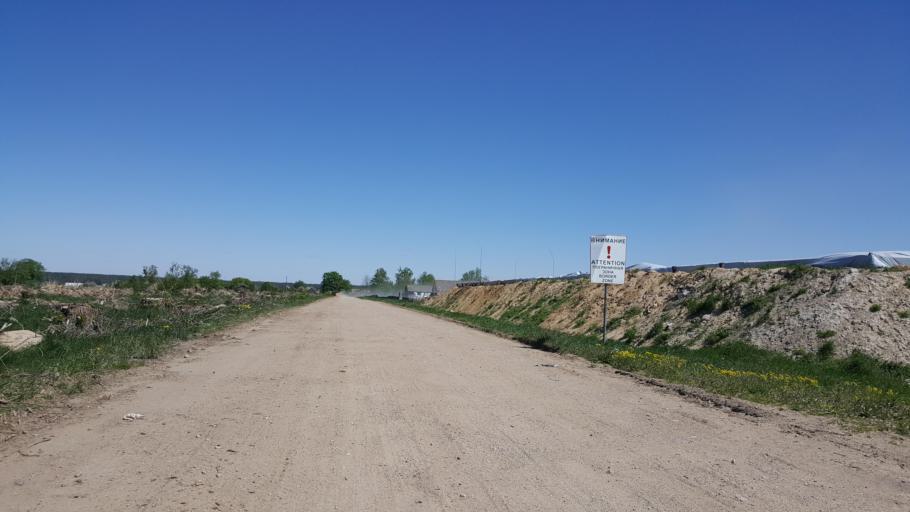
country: BY
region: Brest
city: Kamyanyuki
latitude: 52.4966
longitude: 23.7537
